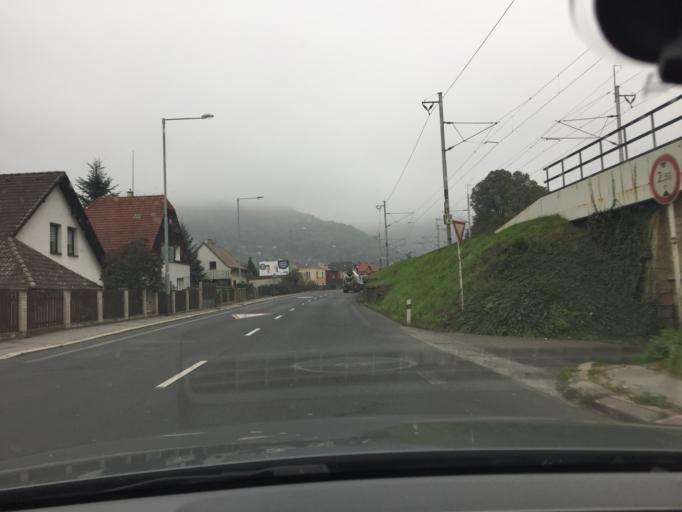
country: CZ
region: Ustecky
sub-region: Okres Usti nad Labem
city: Usti nad Labem
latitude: 50.6235
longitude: 14.0664
